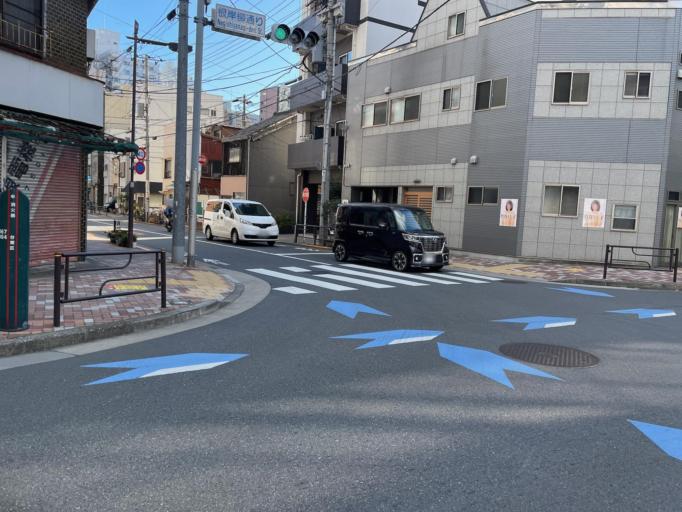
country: JP
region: Saitama
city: Soka
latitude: 35.7241
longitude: 139.7843
